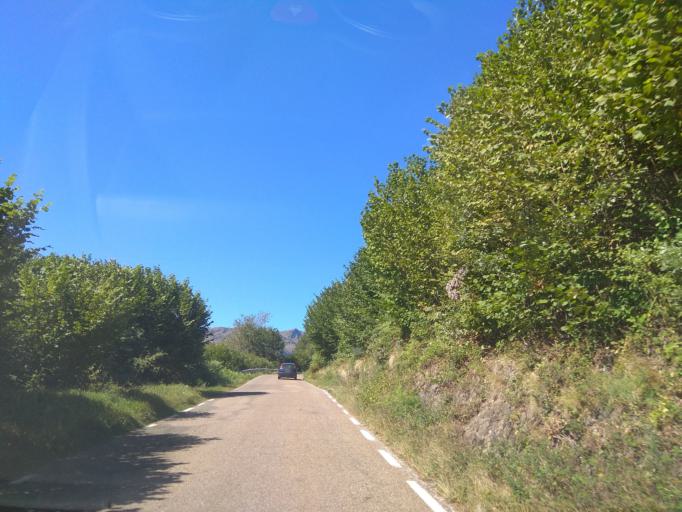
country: ES
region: Catalonia
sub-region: Provincia de Lleida
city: Vielha
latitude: 42.7442
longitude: 0.7425
